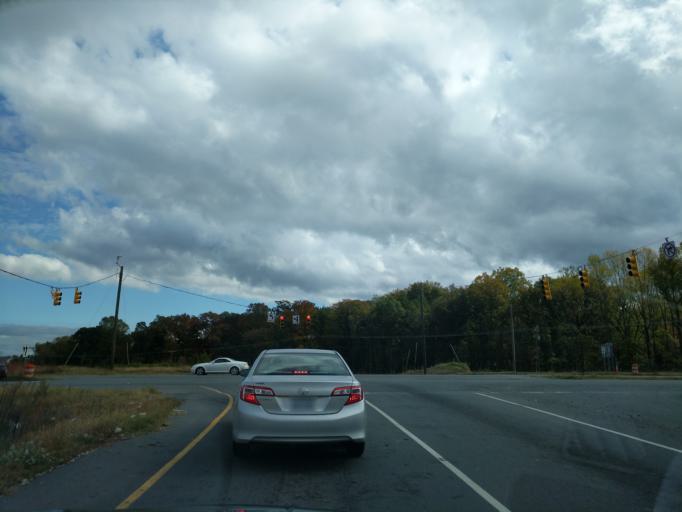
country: US
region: North Carolina
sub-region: Cabarrus County
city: Kannapolis
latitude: 35.4446
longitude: -80.6093
